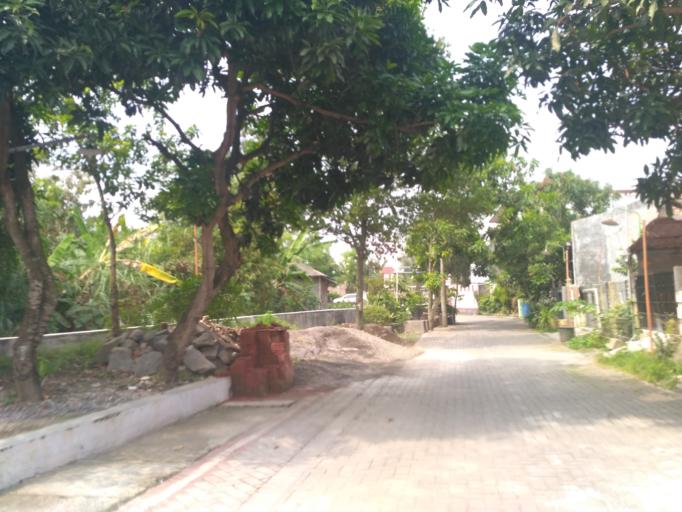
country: ID
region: Central Java
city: Mranggen
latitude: -7.0583
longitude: 110.4702
